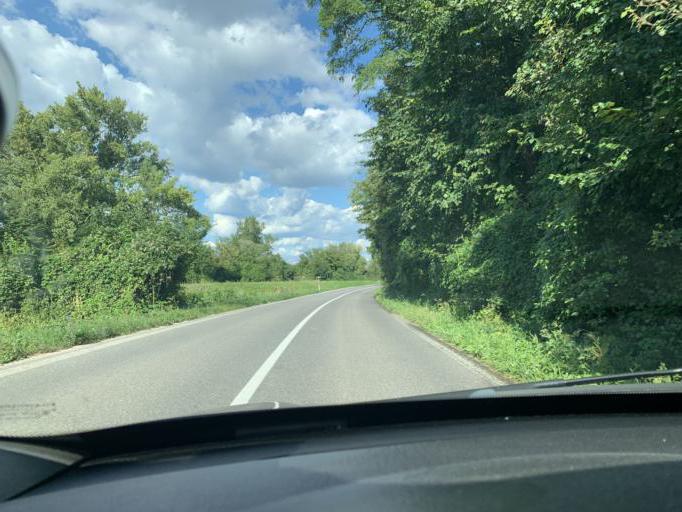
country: SK
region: Trenciansky
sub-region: Okres Nove Mesto nad Vahom
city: Nove Mesto nad Vahom
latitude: 48.8103
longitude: 17.9140
